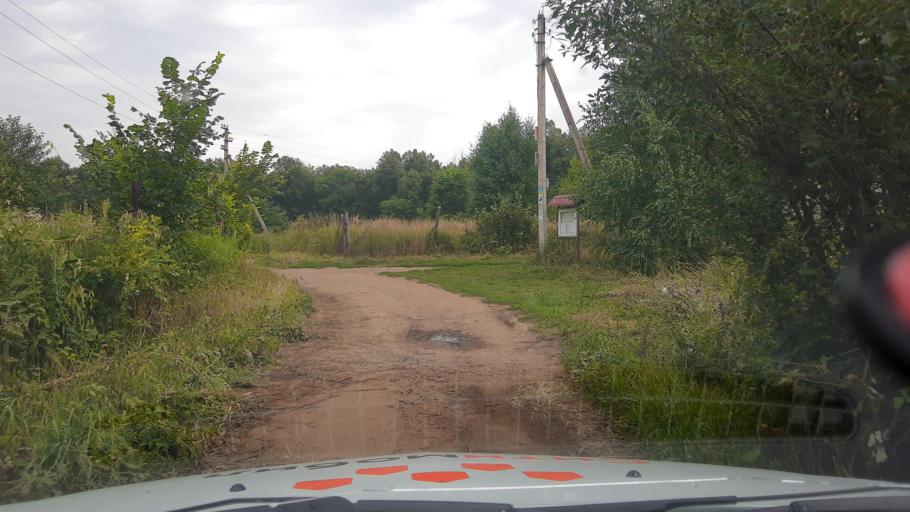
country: RU
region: Bashkortostan
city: Kabakovo
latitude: 54.6691
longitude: 56.0936
